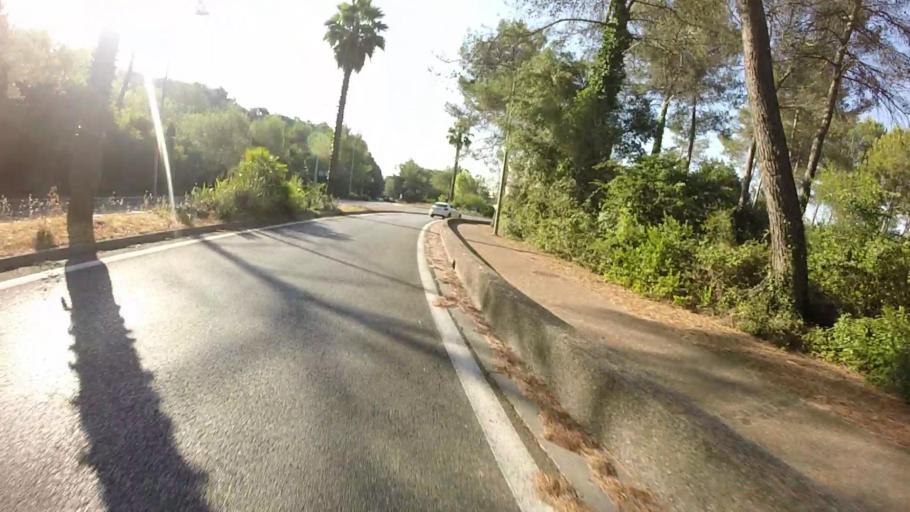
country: FR
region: Provence-Alpes-Cote d'Azur
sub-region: Departement des Alpes-Maritimes
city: Mougins
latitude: 43.6116
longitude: 7.0168
